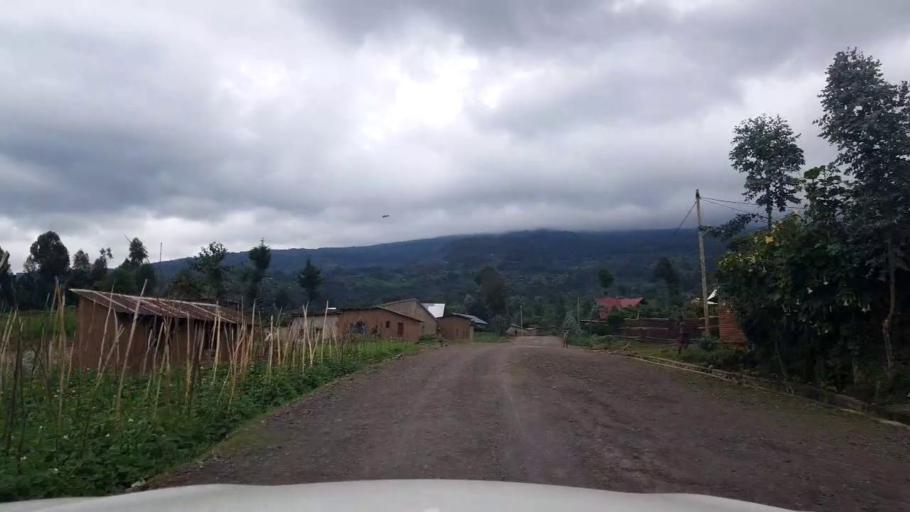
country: RW
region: Northern Province
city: Musanze
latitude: -1.5422
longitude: 29.5330
